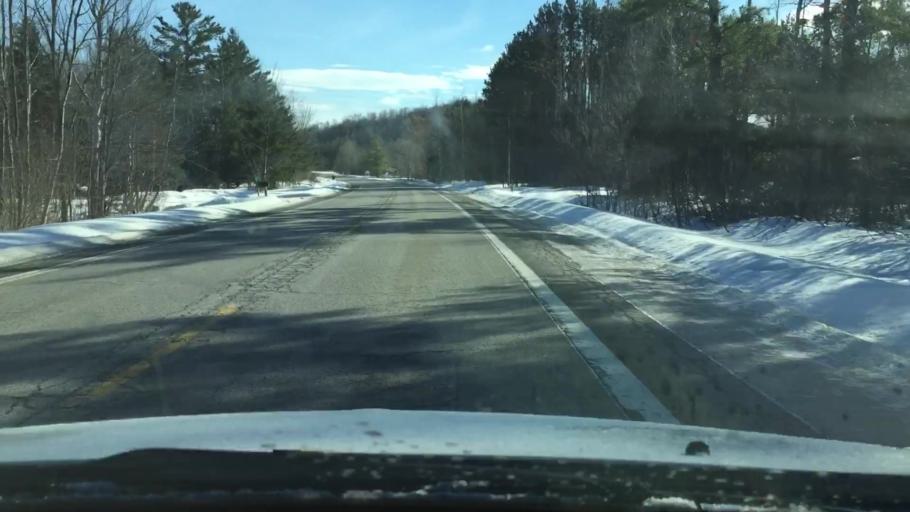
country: US
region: Michigan
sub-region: Charlevoix County
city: East Jordan
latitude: 45.1100
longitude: -85.1281
